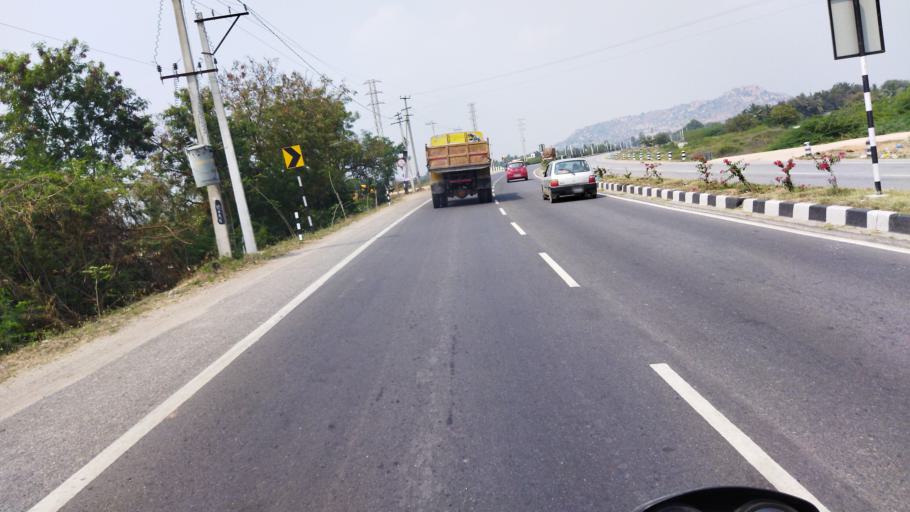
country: IN
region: Telangana
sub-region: Nalgonda
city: Nalgonda
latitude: 17.0799
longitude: 79.2780
